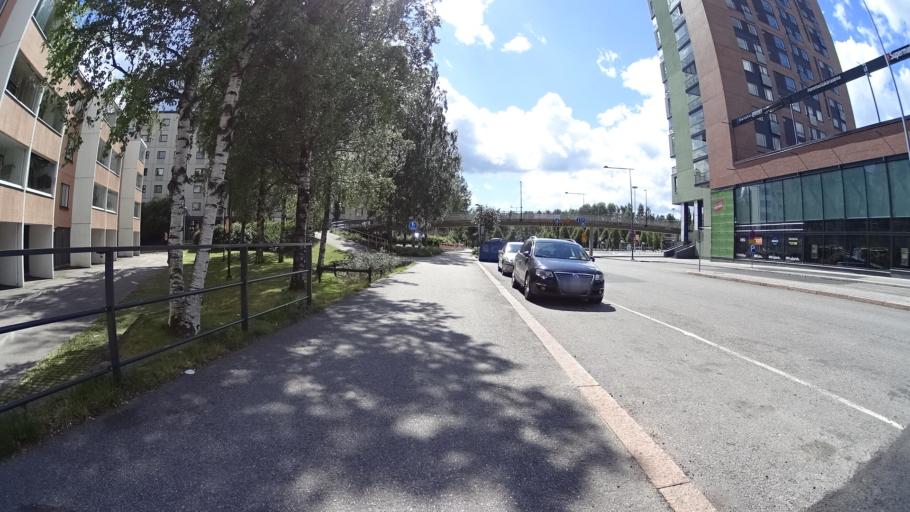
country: FI
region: Uusimaa
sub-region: Helsinki
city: Teekkarikylae
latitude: 60.2784
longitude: 24.8551
